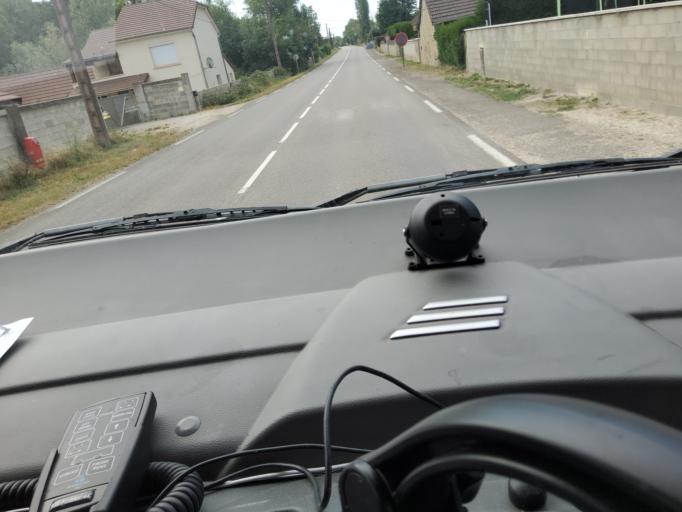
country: FR
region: Franche-Comte
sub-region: Departement du Jura
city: Chaussin
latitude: 46.9306
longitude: 5.5077
